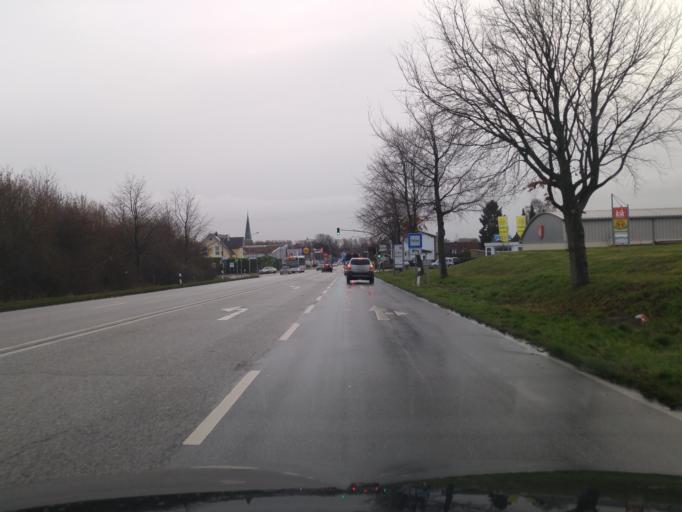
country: DE
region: Schleswig-Holstein
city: Travemuende
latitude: 53.9633
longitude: 10.8593
